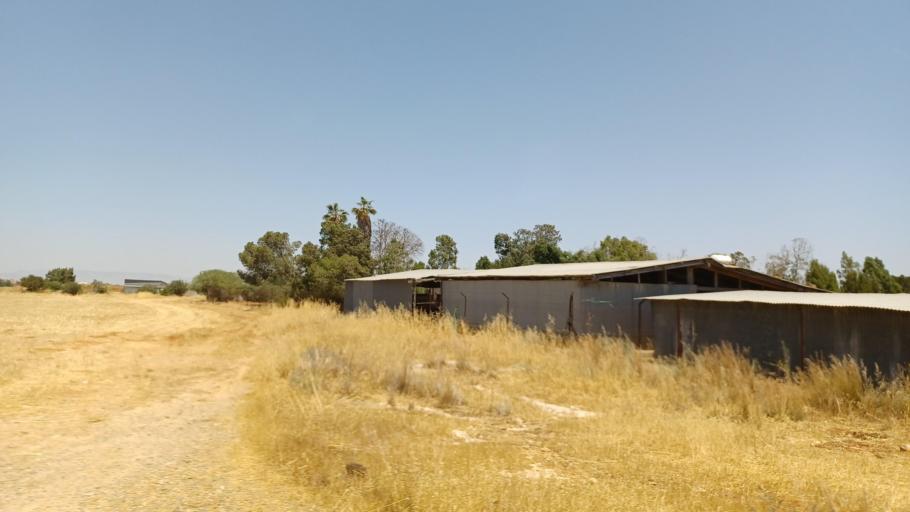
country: CY
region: Larnaka
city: Pergamos
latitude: 35.0242
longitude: 33.7099
